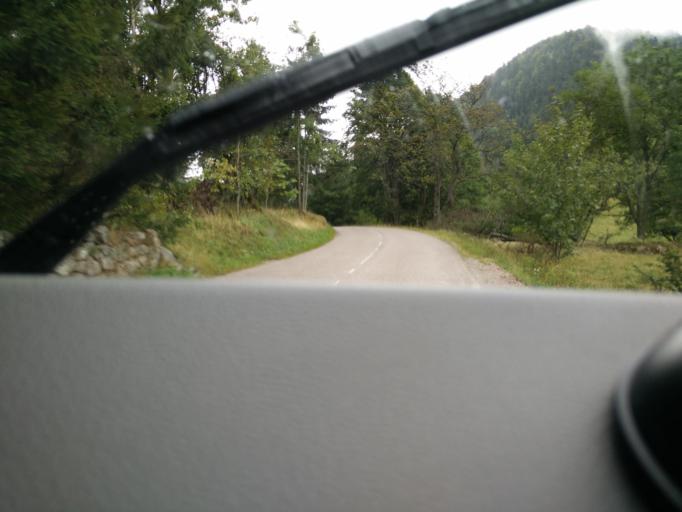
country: FR
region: Lorraine
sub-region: Departement des Vosges
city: Plainfaing
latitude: 48.1015
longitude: 7.0244
